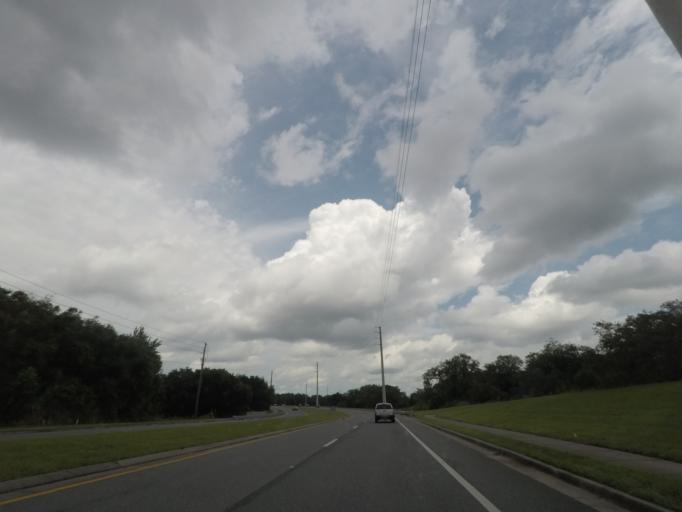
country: US
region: Florida
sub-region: Polk County
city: Citrus Ridge
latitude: 28.3070
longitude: -81.5897
